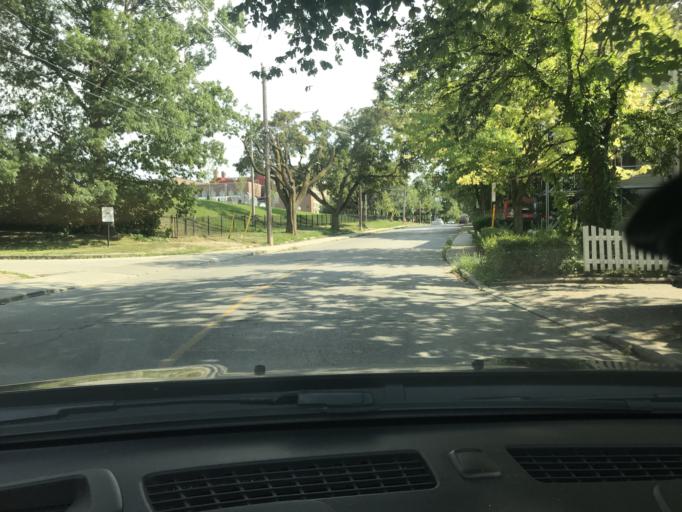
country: CA
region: Ontario
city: Toronto
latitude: 43.7197
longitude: -79.4103
